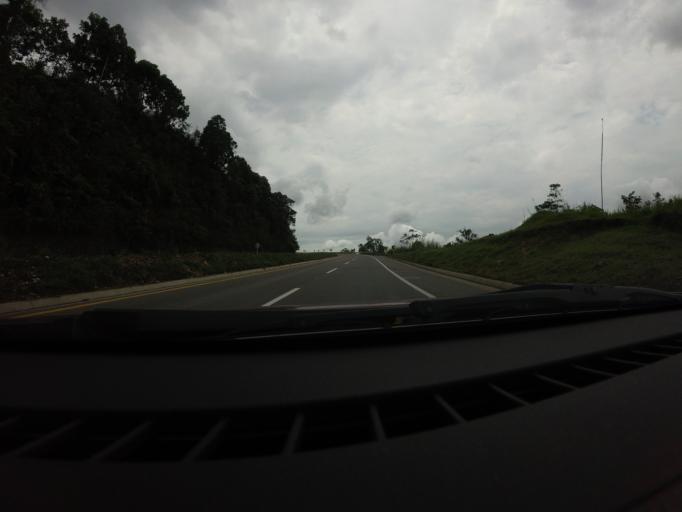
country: CO
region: Cundinamarca
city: La Vega
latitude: 4.9789
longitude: -74.3223
